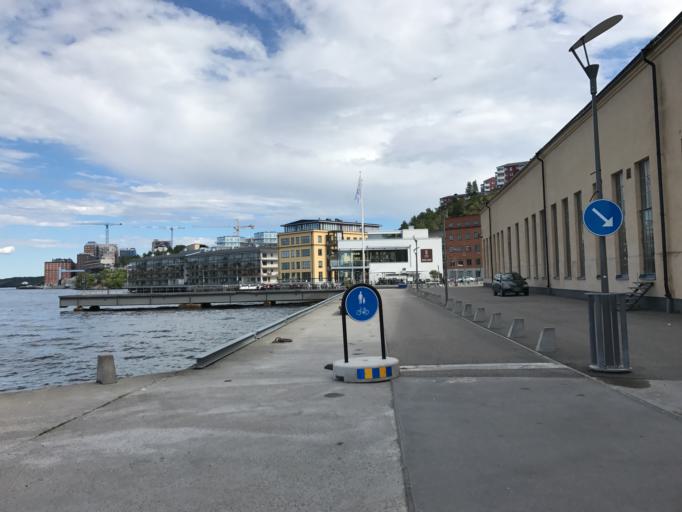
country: SE
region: Stockholm
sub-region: Nacka Kommun
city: Nacka
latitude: 59.3163
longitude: 18.1231
